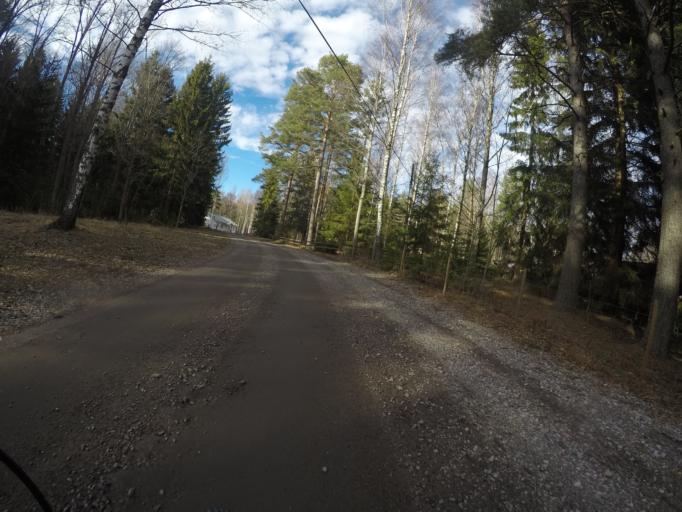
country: SE
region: Vaestmanland
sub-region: Kungsors Kommun
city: Kungsoer
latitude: 59.4315
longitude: 16.1410
